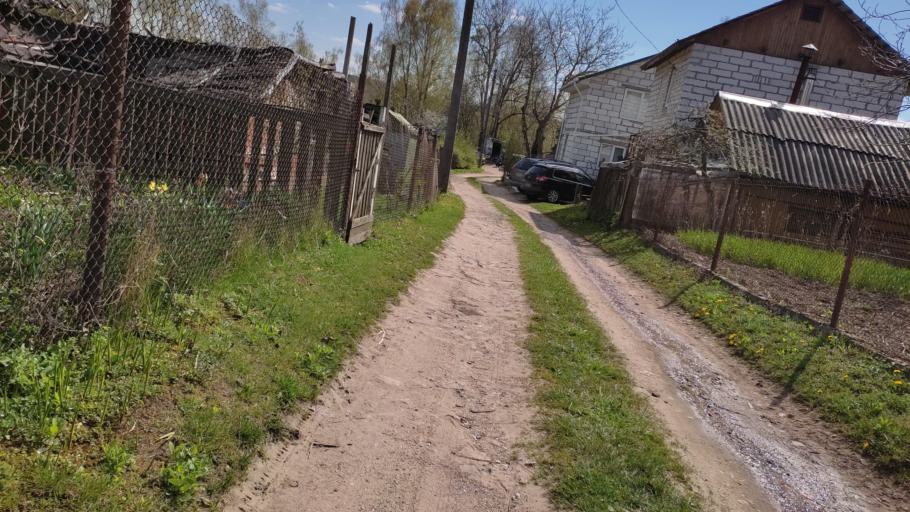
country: BY
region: Grodnenskaya
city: Hrodna
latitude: 53.6563
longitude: 23.8927
